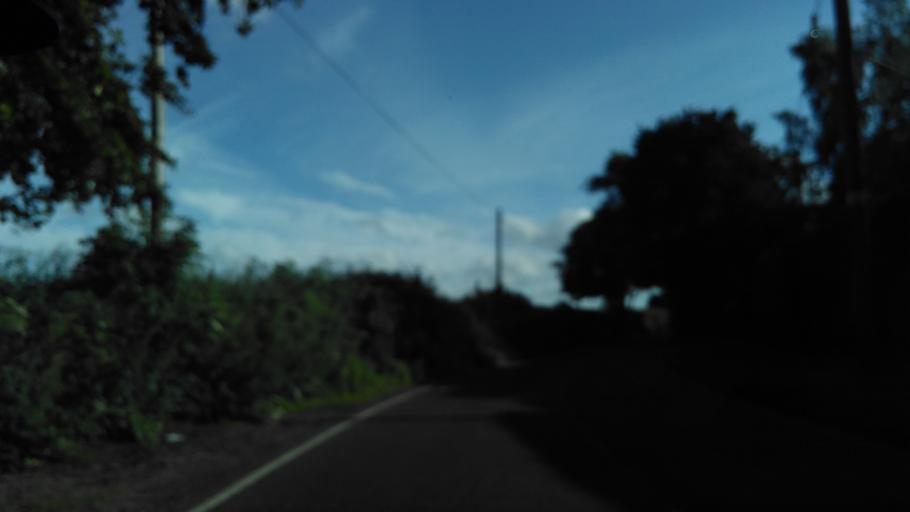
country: GB
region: England
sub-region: Kent
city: Faversham
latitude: 51.2633
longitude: 0.8802
